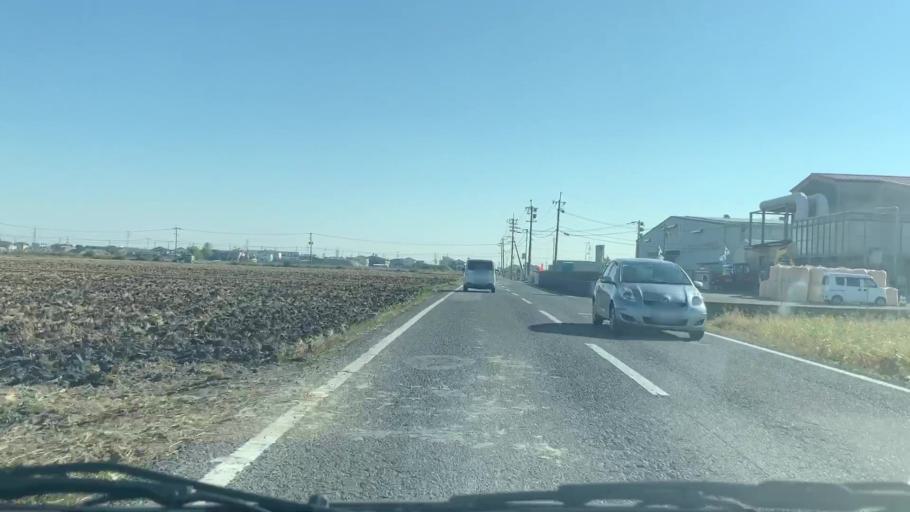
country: JP
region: Saga Prefecture
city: Saga-shi
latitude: 33.2278
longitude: 130.2881
